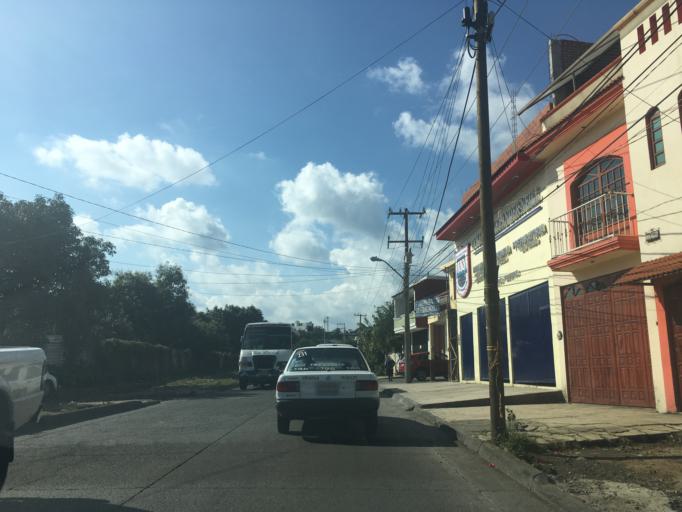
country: MX
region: Michoacan
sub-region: Uruapan
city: Uruapan
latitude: 19.4095
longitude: -102.0688
